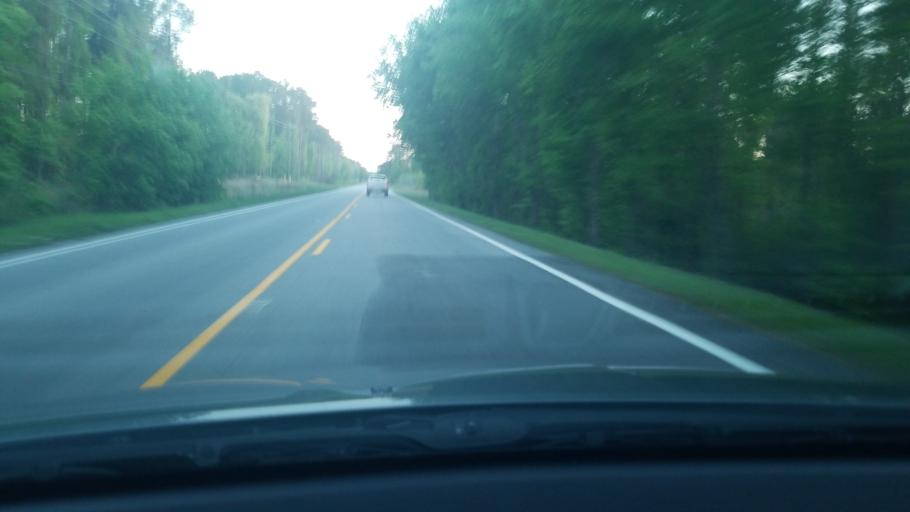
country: US
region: North Carolina
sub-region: Craven County
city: Vanceboro
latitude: 35.2256
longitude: -77.1196
